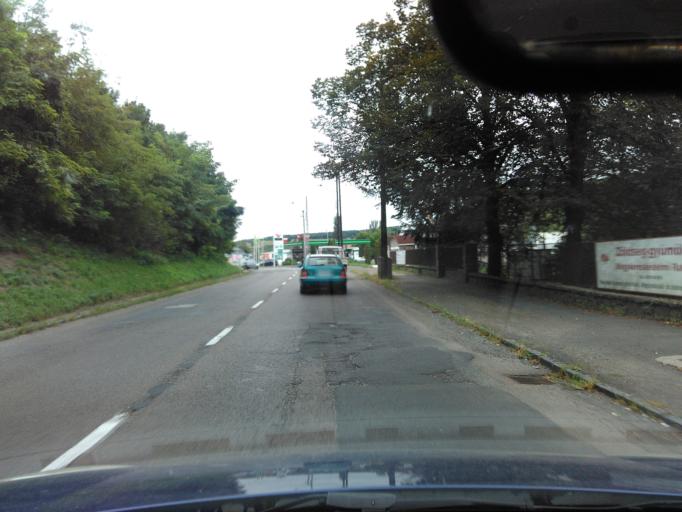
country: HU
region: Nograd
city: Salgotarjan
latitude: 48.0917
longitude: 19.7962
